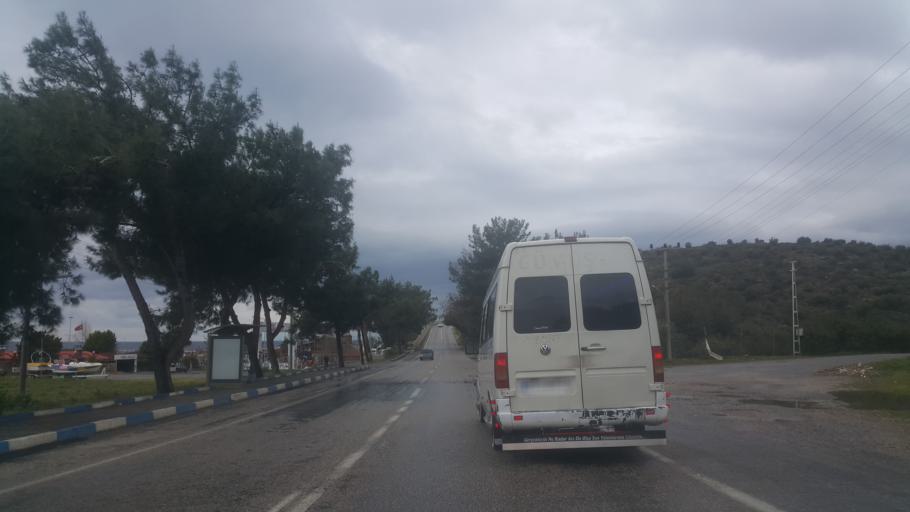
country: TR
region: Izmir
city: Ozdere
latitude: 38.0108
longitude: 27.1085
